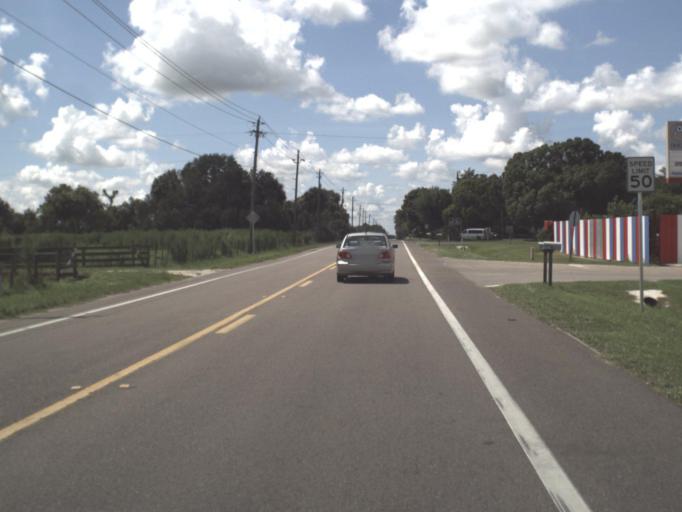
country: US
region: Florida
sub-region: DeSoto County
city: Southeast Arcadia
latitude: 27.1897
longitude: -81.8687
